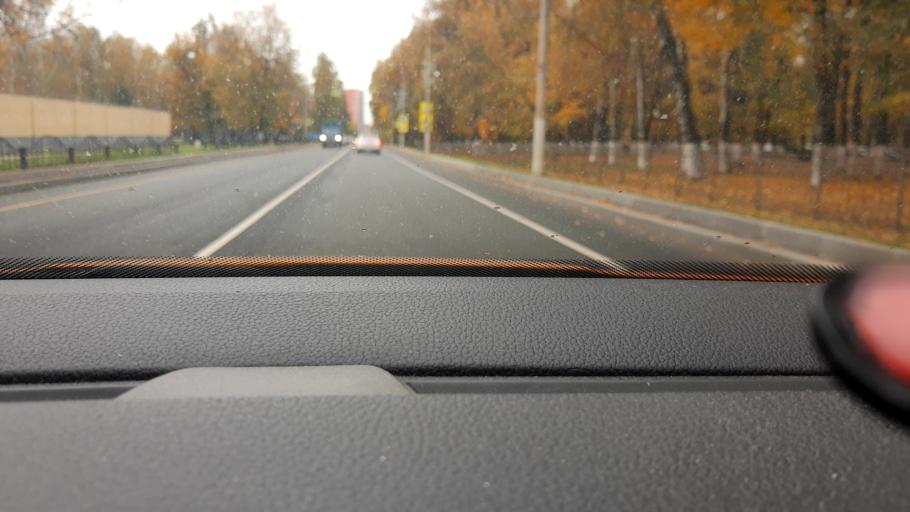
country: RU
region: Moskovskaya
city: Krasnogorsk
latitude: 55.8256
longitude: 37.3354
